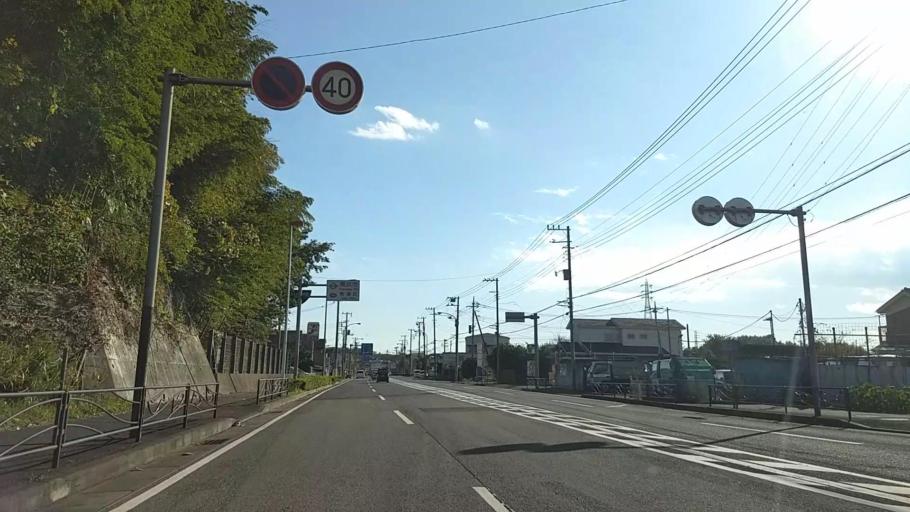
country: JP
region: Tokyo
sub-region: Machida-shi
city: Machida
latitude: 35.5682
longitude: 139.5137
